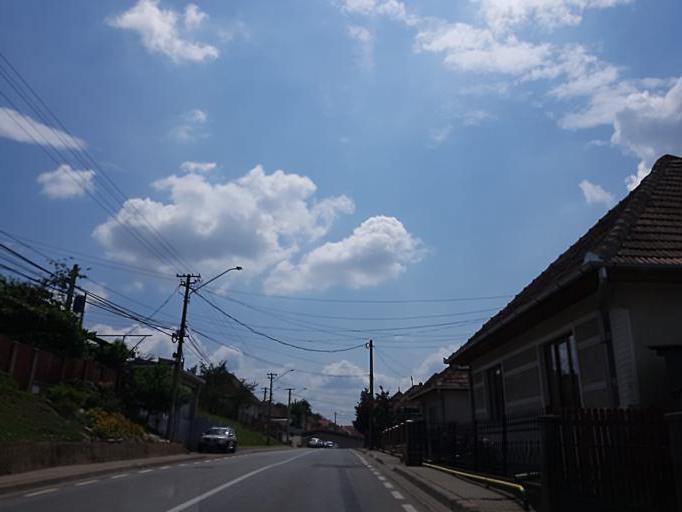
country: RO
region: Alba
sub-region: Municipiul Blaj
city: Veza
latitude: 46.1738
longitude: 23.9393
